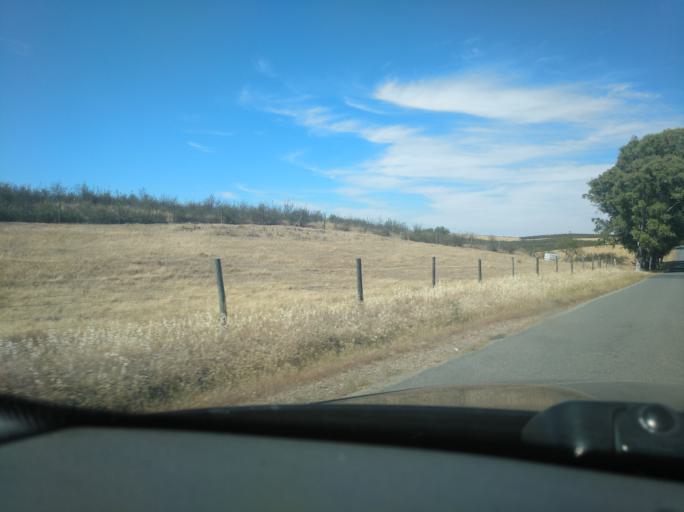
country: PT
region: Beja
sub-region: Mertola
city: Mertola
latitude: 37.6195
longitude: -7.7451
